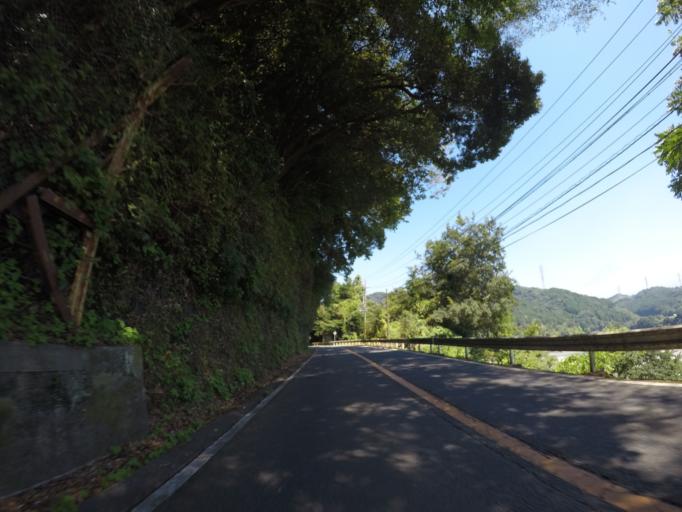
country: JP
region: Shizuoka
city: Fujinomiya
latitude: 35.1774
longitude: 138.6139
